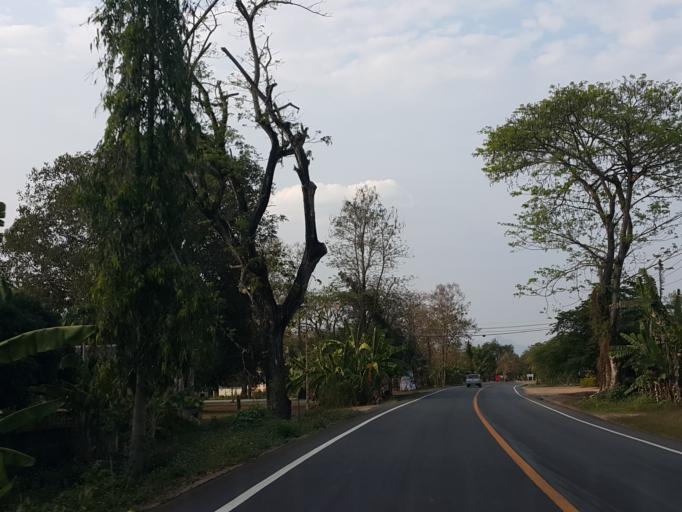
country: TH
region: Lampang
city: Lampang
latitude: 18.4888
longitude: 99.4721
